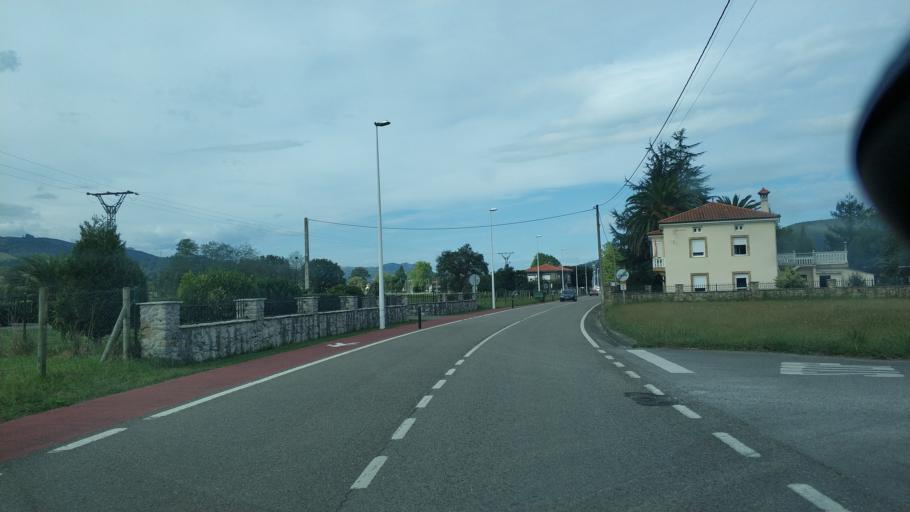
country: ES
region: Cantabria
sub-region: Provincia de Cantabria
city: Santa Maria de Cayon
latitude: 43.3090
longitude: -3.8645
